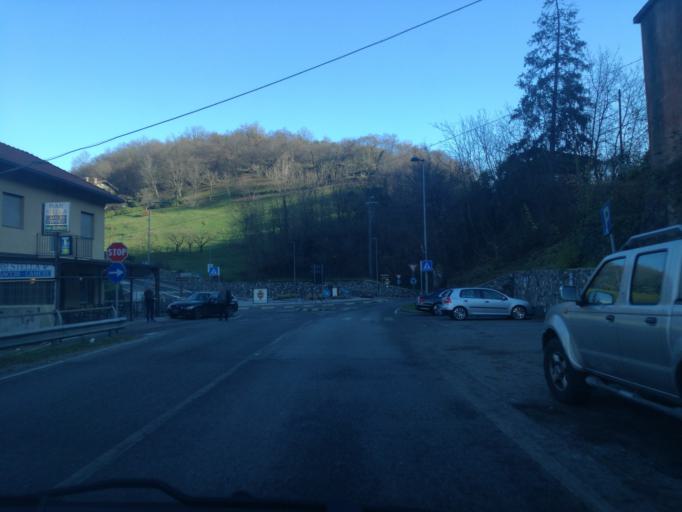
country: IT
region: Lombardy
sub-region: Provincia di Bergamo
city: Castro
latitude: 45.8070
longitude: 10.0599
